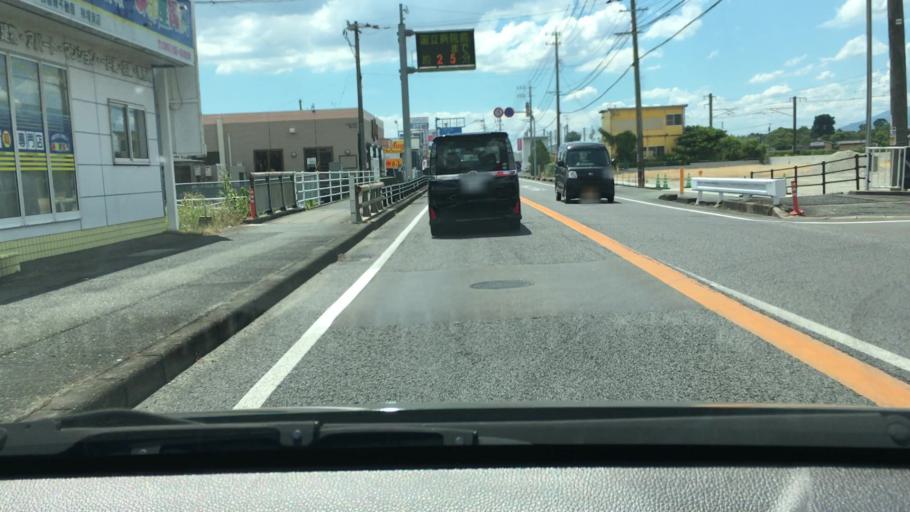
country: JP
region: Saga Prefecture
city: Kanzakimachi-kanzaki
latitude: 33.3225
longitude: 130.3957
